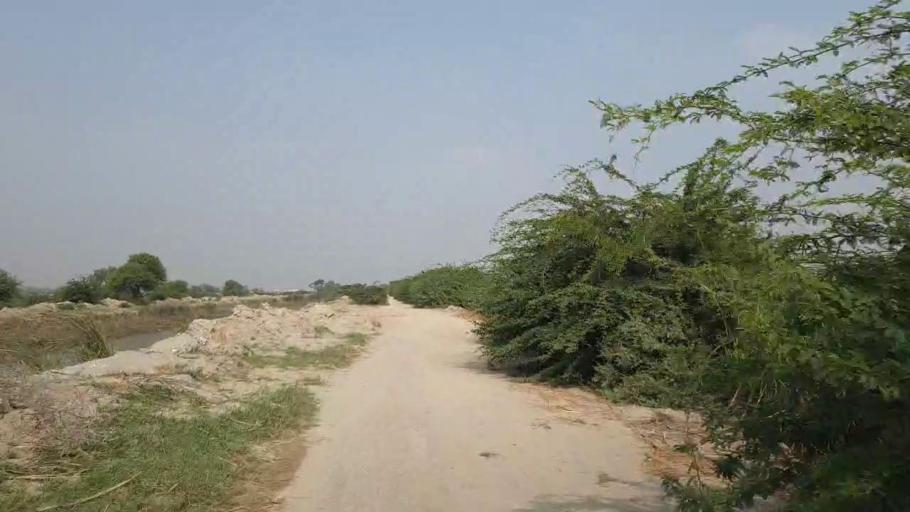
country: PK
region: Sindh
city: Kario
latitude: 24.7770
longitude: 68.5220
